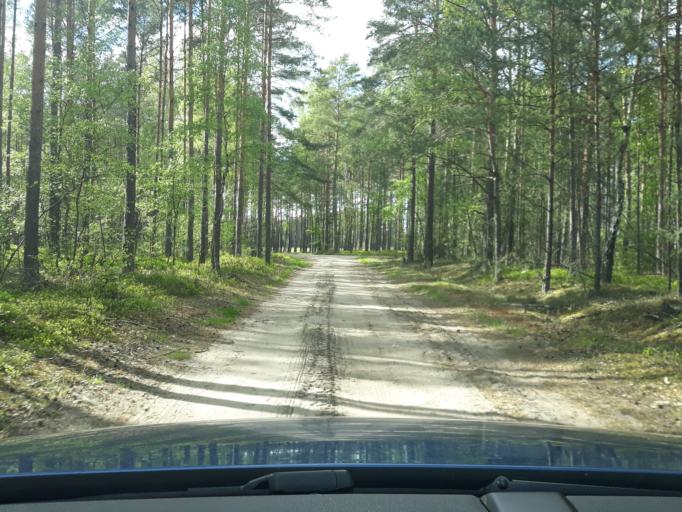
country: PL
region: Pomeranian Voivodeship
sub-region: Powiat czluchowski
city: Czluchow
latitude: 53.7197
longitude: 17.3331
